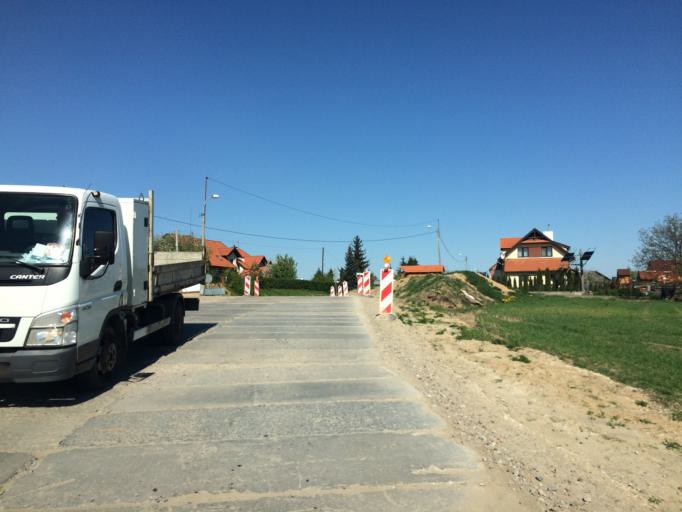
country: PL
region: Warmian-Masurian Voivodeship
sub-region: Powiat ostrodzki
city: Ostroda
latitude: 53.6766
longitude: 19.9825
